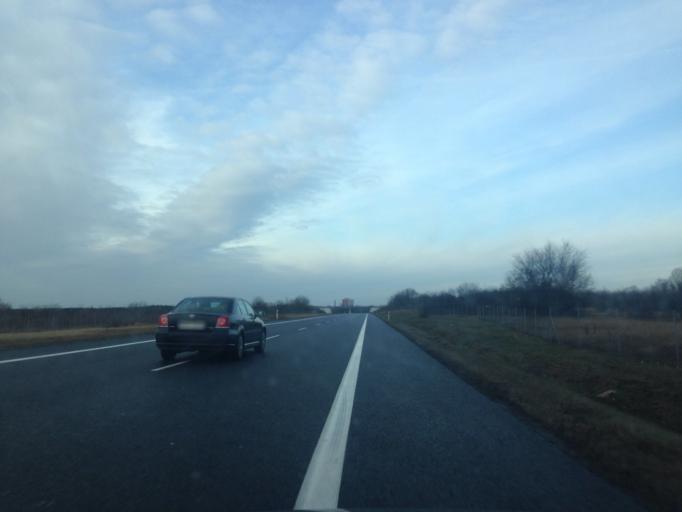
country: PL
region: Kujawsko-Pomorskie
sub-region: Torun
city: Torun
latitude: 52.9835
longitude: 18.5985
